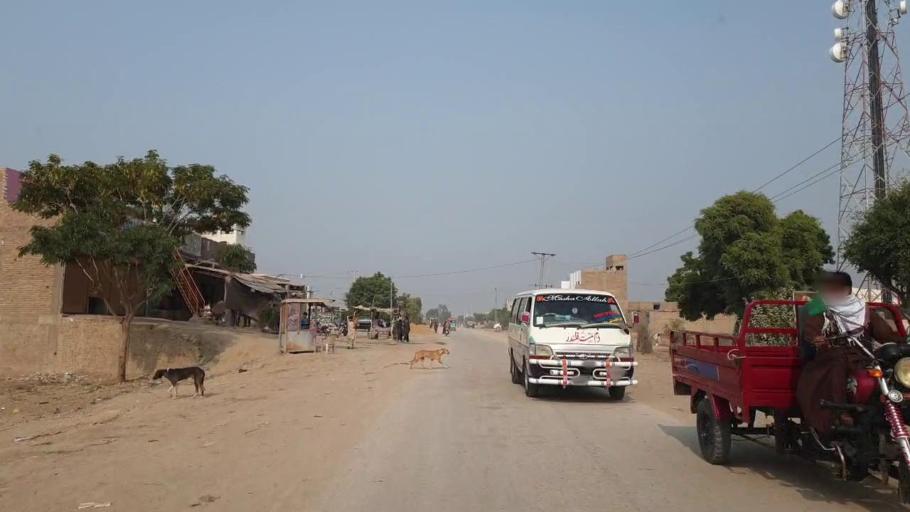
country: PK
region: Sindh
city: Bhan
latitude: 26.5639
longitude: 67.7234
